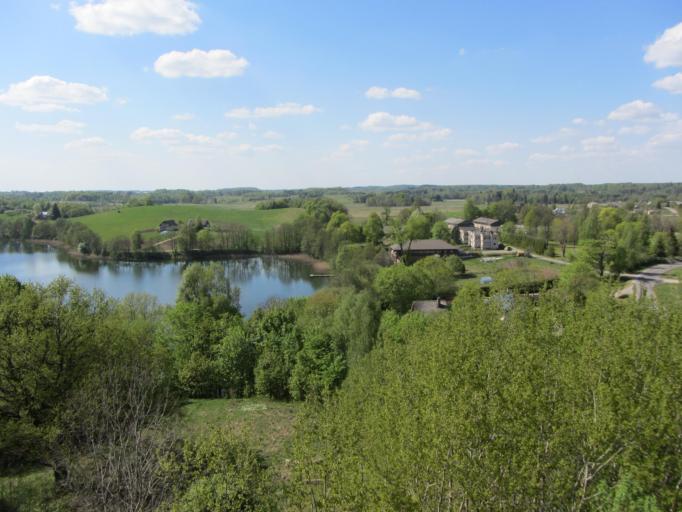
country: LT
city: Moletai
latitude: 55.1132
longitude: 25.4001
